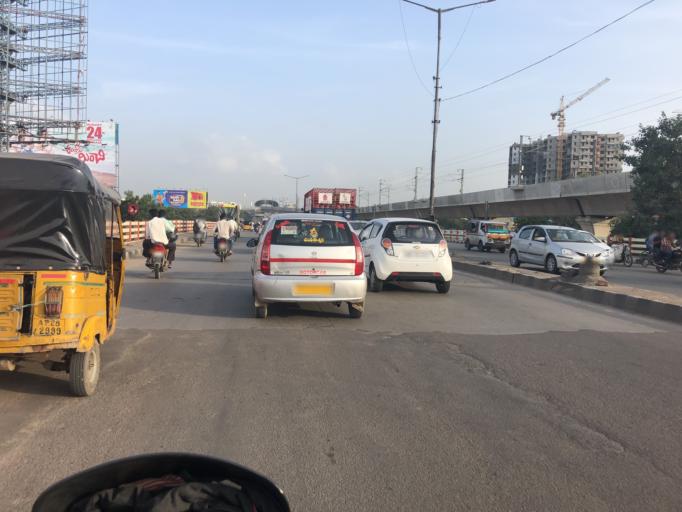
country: IN
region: Telangana
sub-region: Rangareddi
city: Kukatpalli
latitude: 17.4621
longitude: 78.4313
